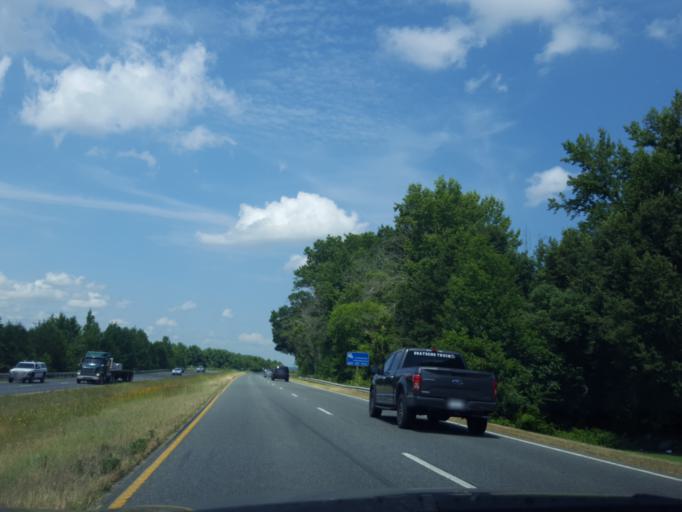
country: US
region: Virginia
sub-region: King George County
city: Passapatanzy
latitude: 38.2565
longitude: -77.3853
